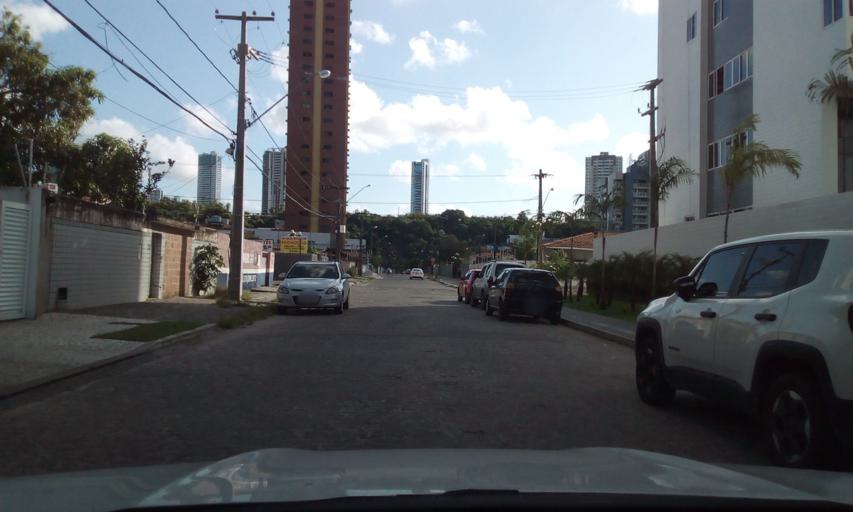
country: BR
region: Paraiba
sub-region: Joao Pessoa
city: Joao Pessoa
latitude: -7.1083
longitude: -34.8347
